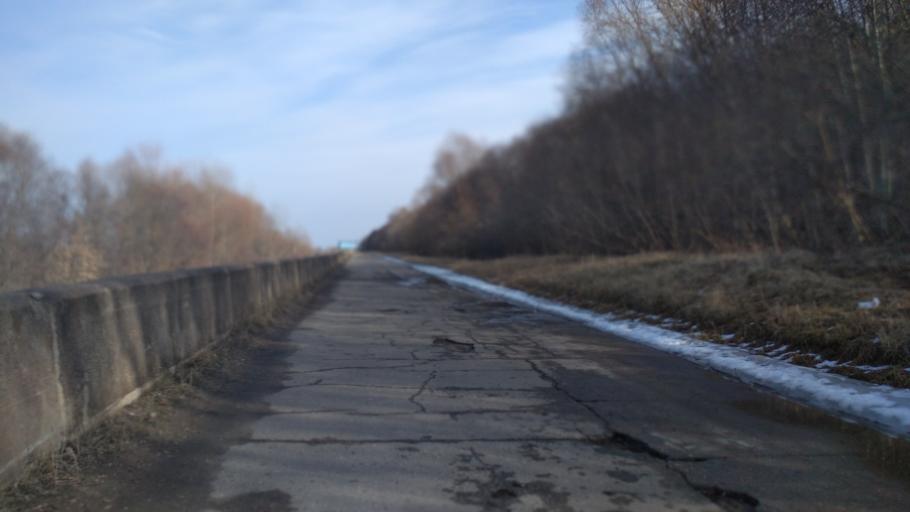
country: RU
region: Chuvashia
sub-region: Cheboksarskiy Rayon
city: Cheboksary
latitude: 56.1458
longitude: 47.3138
